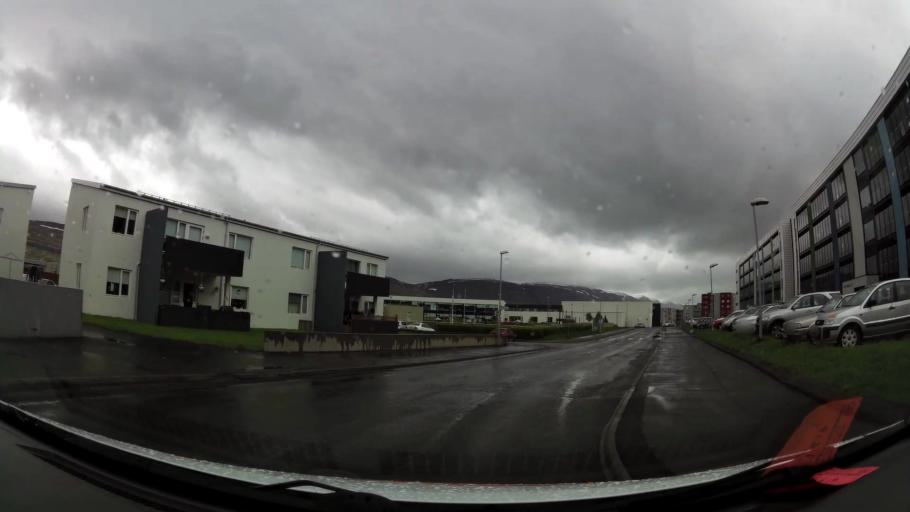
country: IS
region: Northeast
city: Akureyri
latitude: 65.6657
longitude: -18.1025
